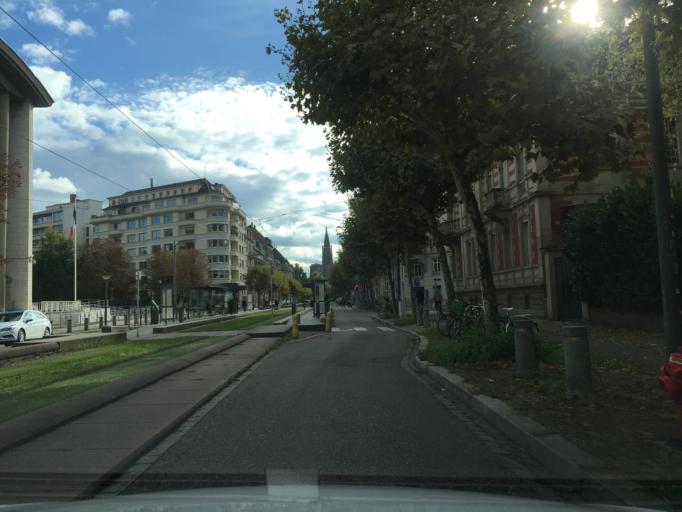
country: FR
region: Alsace
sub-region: Departement du Bas-Rhin
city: Strasbourg
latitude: 48.5908
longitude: 7.7562
